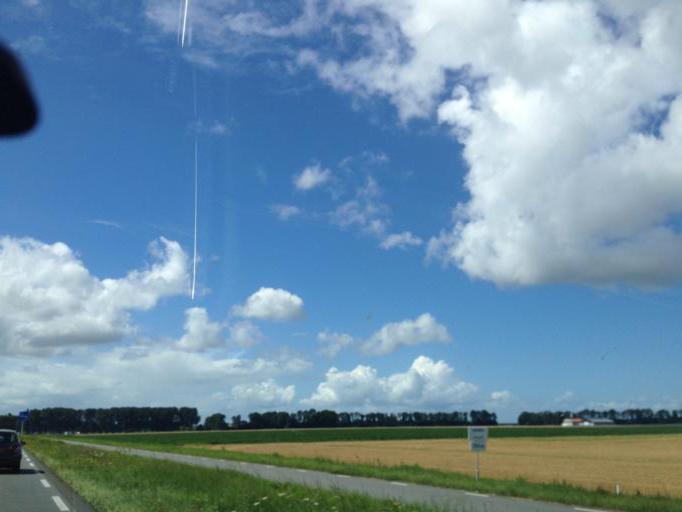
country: NL
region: Flevoland
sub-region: Gemeente Dronten
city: Dronten
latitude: 52.5376
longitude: 5.7485
